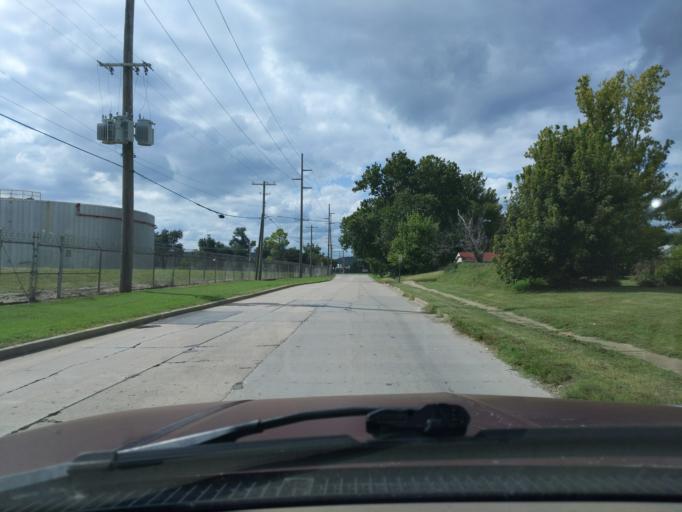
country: US
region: Oklahoma
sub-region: Tulsa County
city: Tulsa
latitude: 36.1263
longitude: -96.0045
